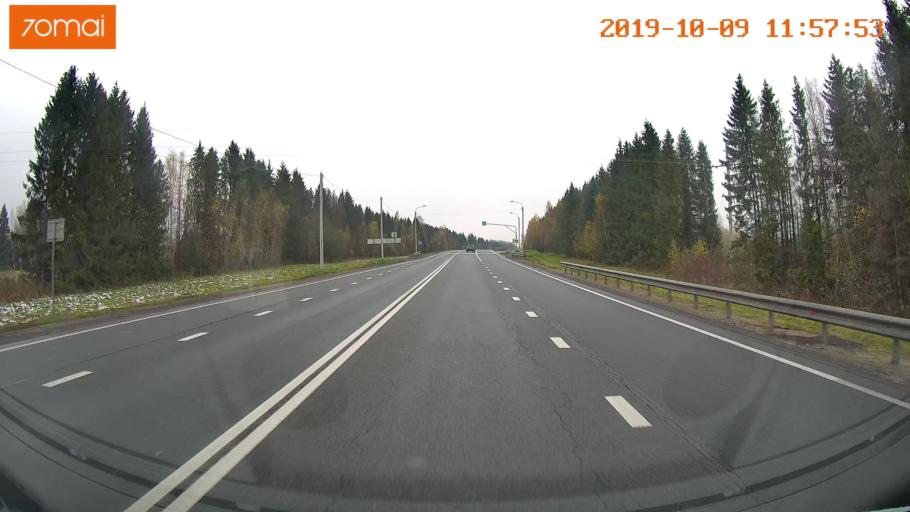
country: RU
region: Vologda
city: Gryazovets
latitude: 58.7260
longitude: 40.2951
